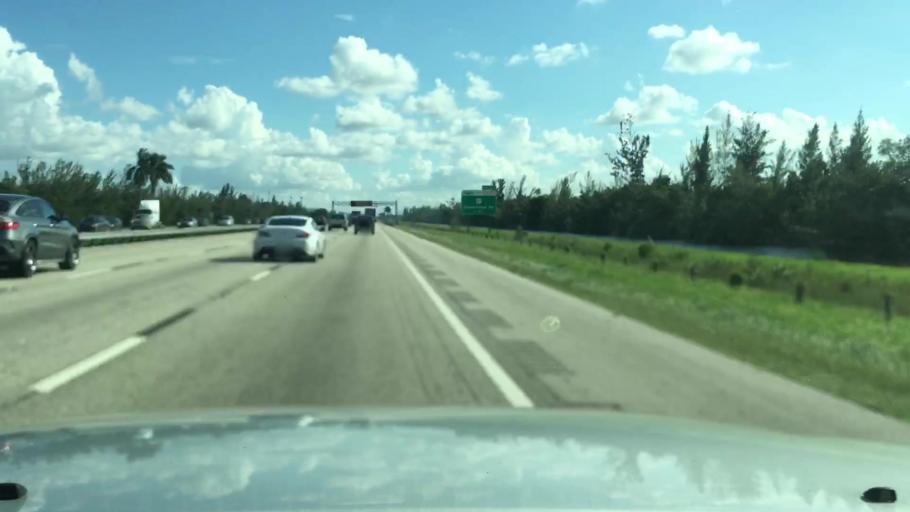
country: US
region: Florida
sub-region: Miami-Dade County
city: Palm Springs North
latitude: 25.9219
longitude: -80.3759
